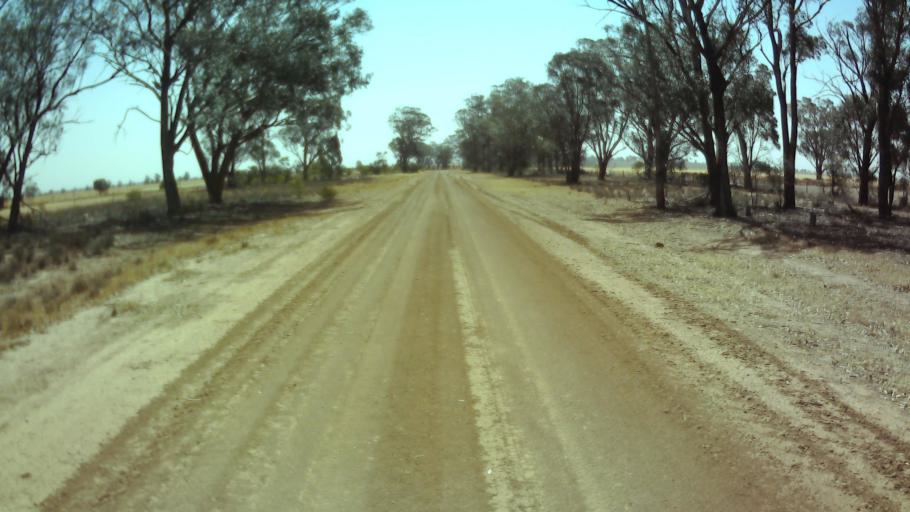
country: AU
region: New South Wales
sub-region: Weddin
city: Grenfell
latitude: -33.9229
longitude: 147.7834
